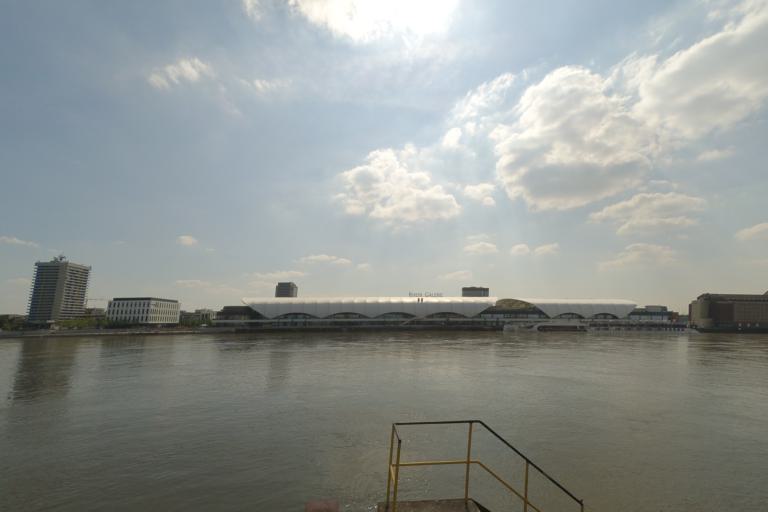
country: DE
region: Rheinland-Pfalz
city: Ludwigshafen am Rhein
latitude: 49.4873
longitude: 8.4509
